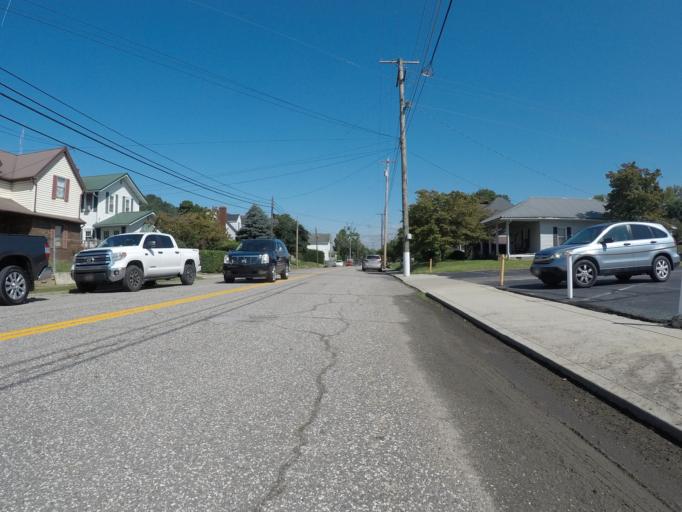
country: US
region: Kentucky
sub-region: Boyd County
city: Catlettsburg
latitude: 38.4078
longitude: -82.5987
